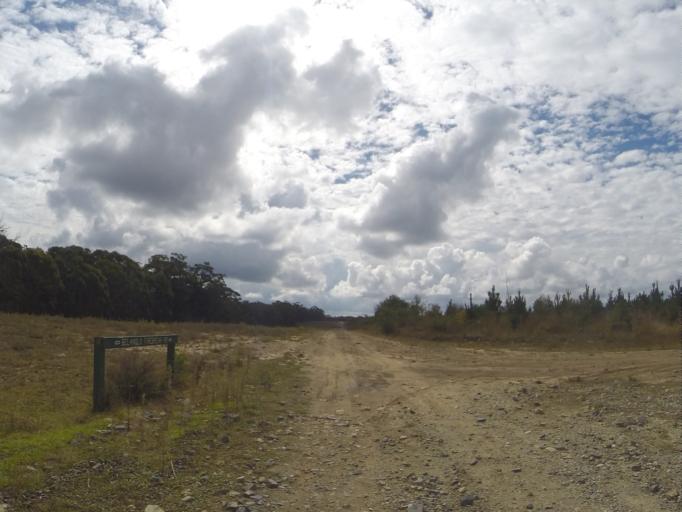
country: AU
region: New South Wales
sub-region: Wingecarribee
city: Moss Vale
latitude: -34.5122
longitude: 150.2274
